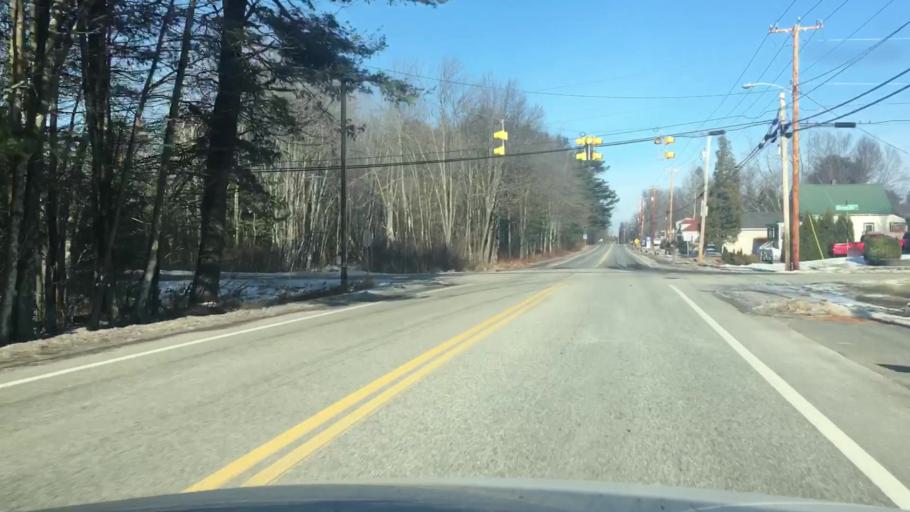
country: US
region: Maine
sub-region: Androscoggin County
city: Auburn
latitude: 44.0875
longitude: -70.2624
